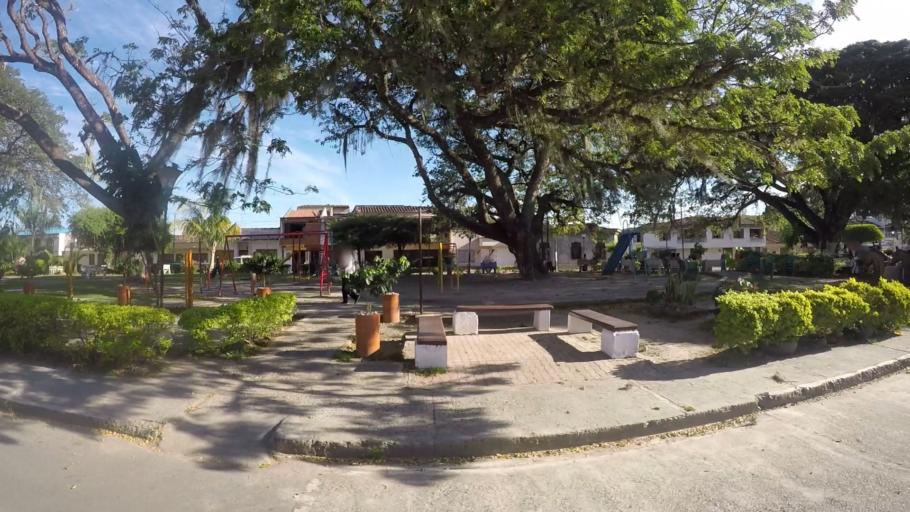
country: CO
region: Valle del Cauca
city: Cartago
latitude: 4.7521
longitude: -75.9215
